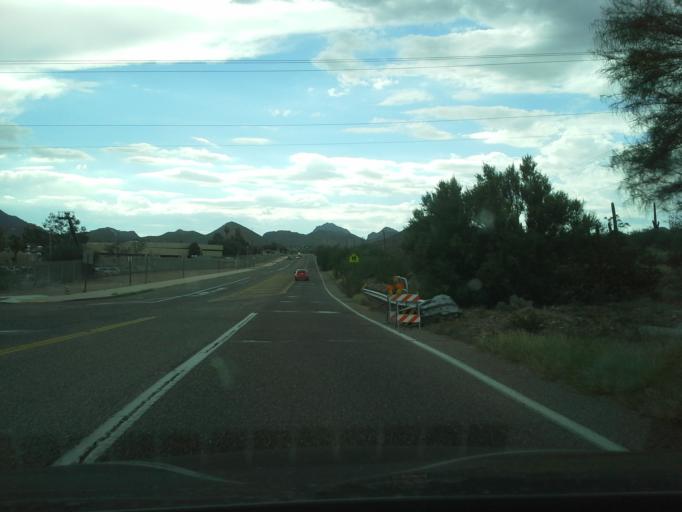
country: US
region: Arizona
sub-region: Pima County
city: South Tucson
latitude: 32.2069
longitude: -111.0073
